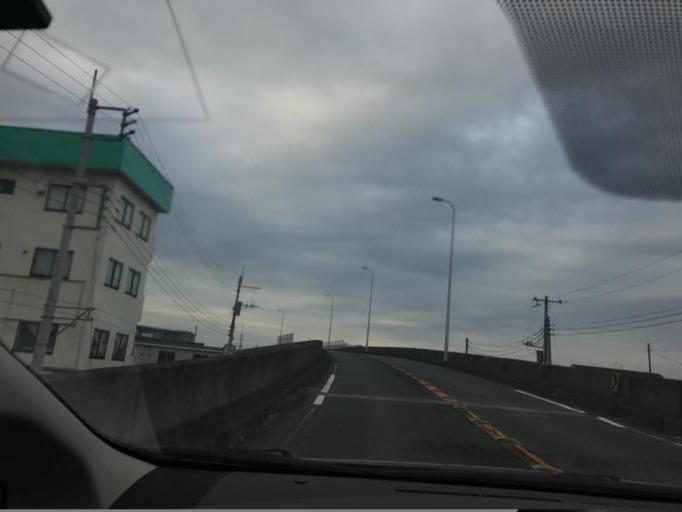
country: JP
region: Ibaraki
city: Mitsukaido
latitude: 36.0168
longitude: 139.9886
